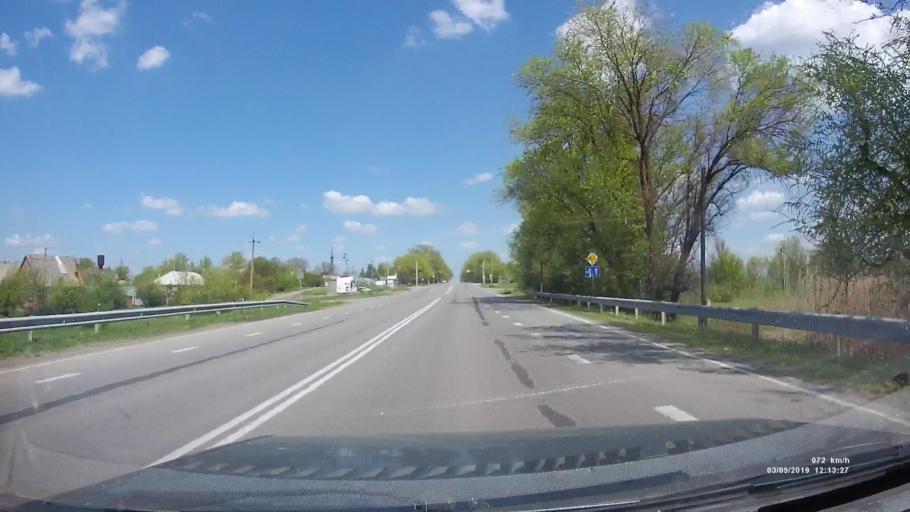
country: RU
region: Rostov
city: Melikhovskaya
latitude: 47.3328
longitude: 40.5551
